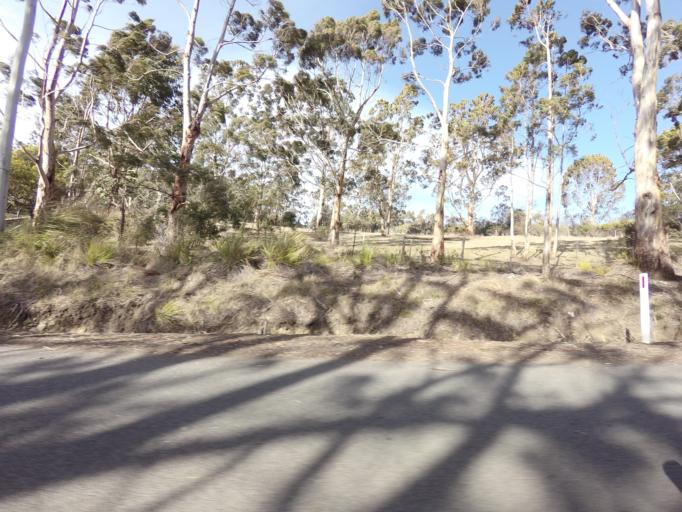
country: AU
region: Tasmania
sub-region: Kingborough
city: Kettering
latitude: -43.1656
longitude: 147.2189
